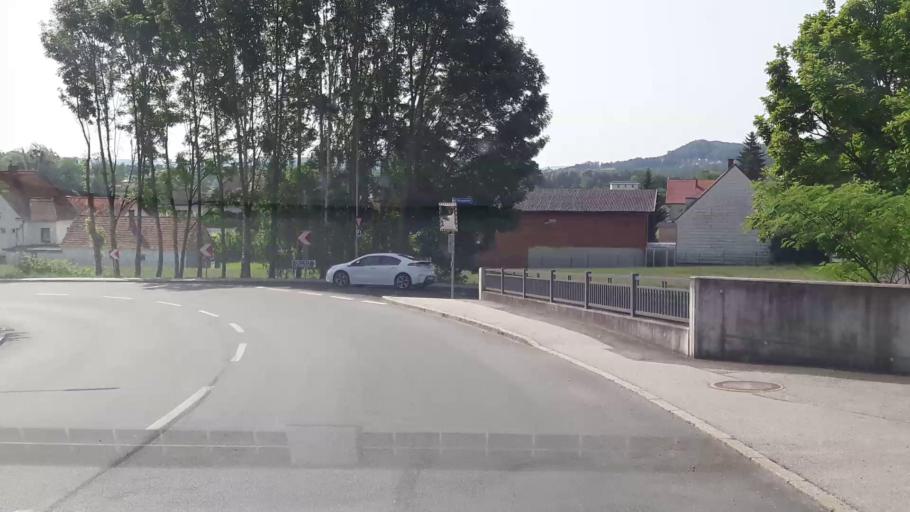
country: AT
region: Burgenland
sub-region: Politischer Bezirk Gussing
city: Stegersbach
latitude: 47.1590
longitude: 16.1592
